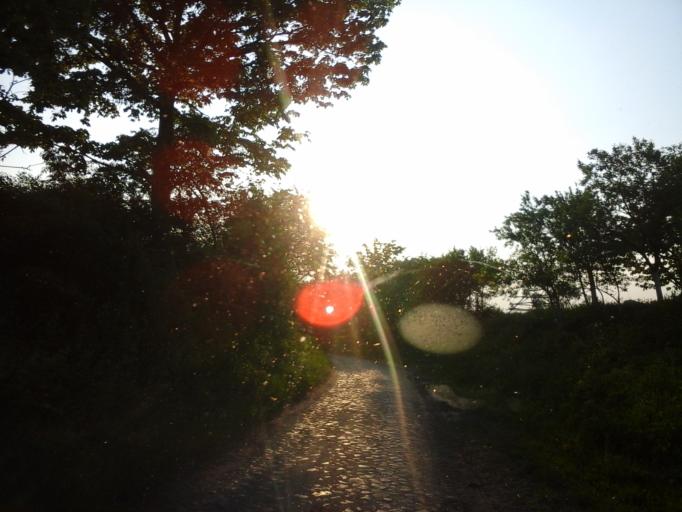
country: PL
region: West Pomeranian Voivodeship
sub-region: Powiat choszczenski
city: Bierzwnik
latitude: 52.9901
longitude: 15.6291
